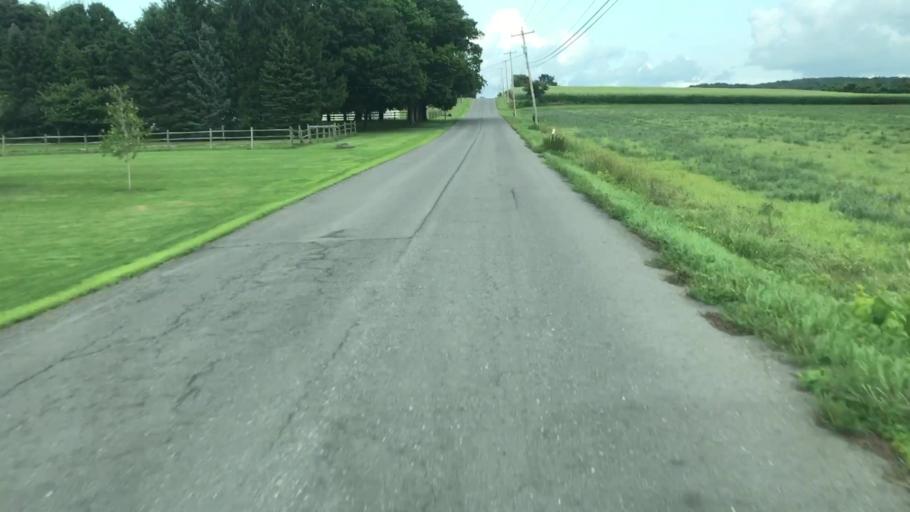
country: US
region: New York
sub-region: Onondaga County
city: Elbridge
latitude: 42.9851
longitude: -76.5031
